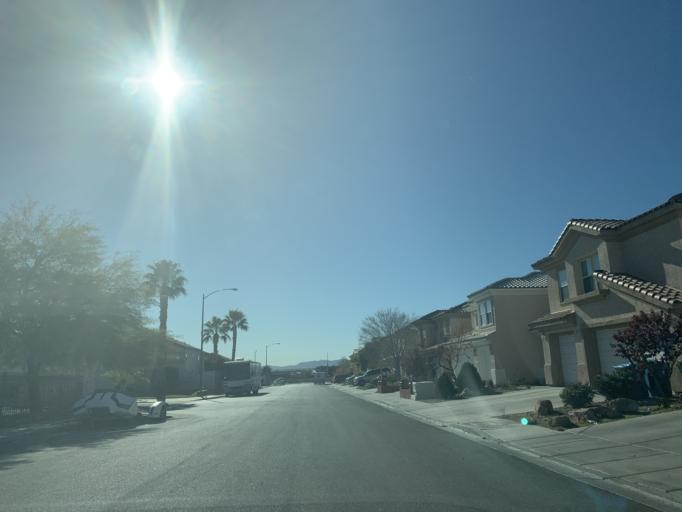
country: US
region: Nevada
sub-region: Clark County
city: Spring Valley
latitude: 36.1201
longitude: -115.2858
